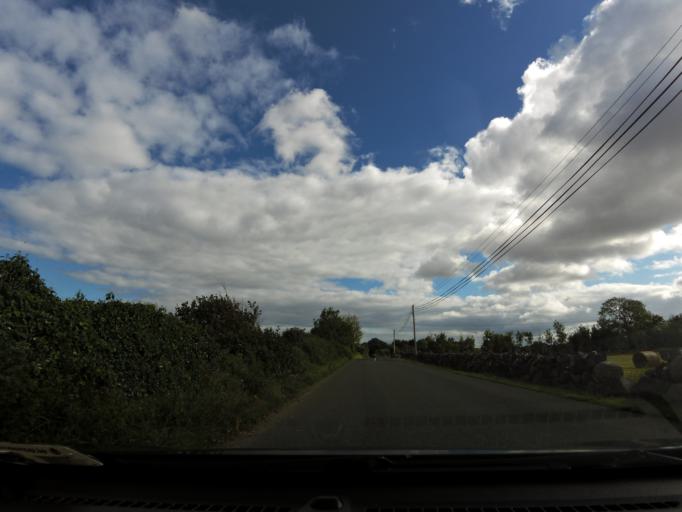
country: IE
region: Connaught
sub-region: County Galway
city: Moycullen
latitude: 53.3564
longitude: -9.1749
